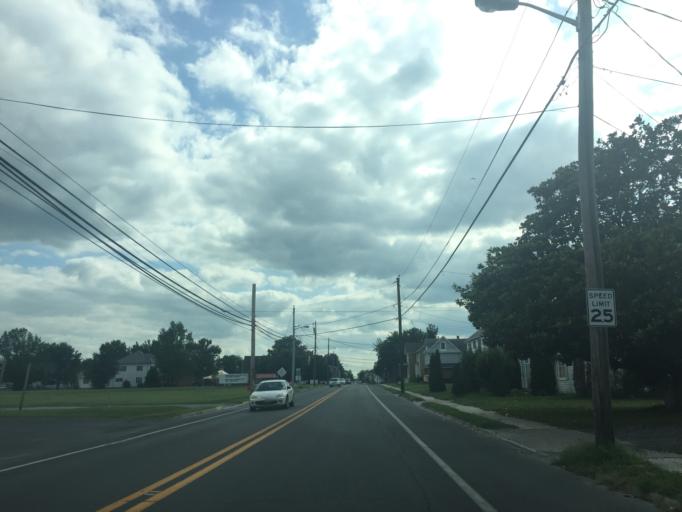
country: US
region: Delaware
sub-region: Sussex County
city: Georgetown
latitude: 38.6948
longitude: -75.3797
